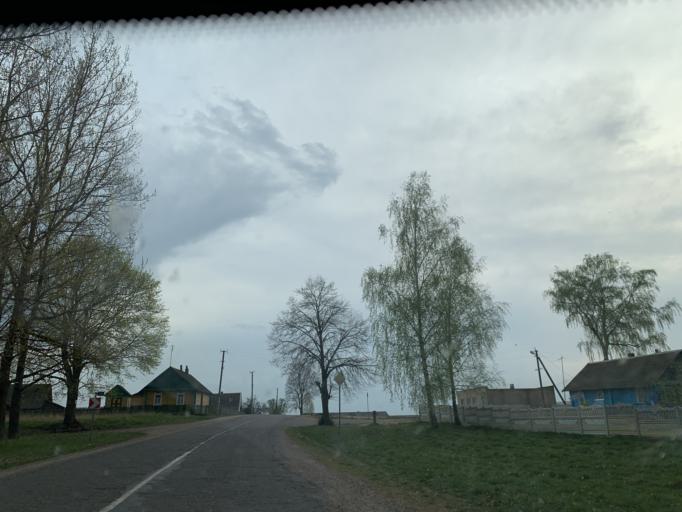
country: BY
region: Minsk
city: Kapyl'
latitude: 53.2946
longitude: 27.0344
